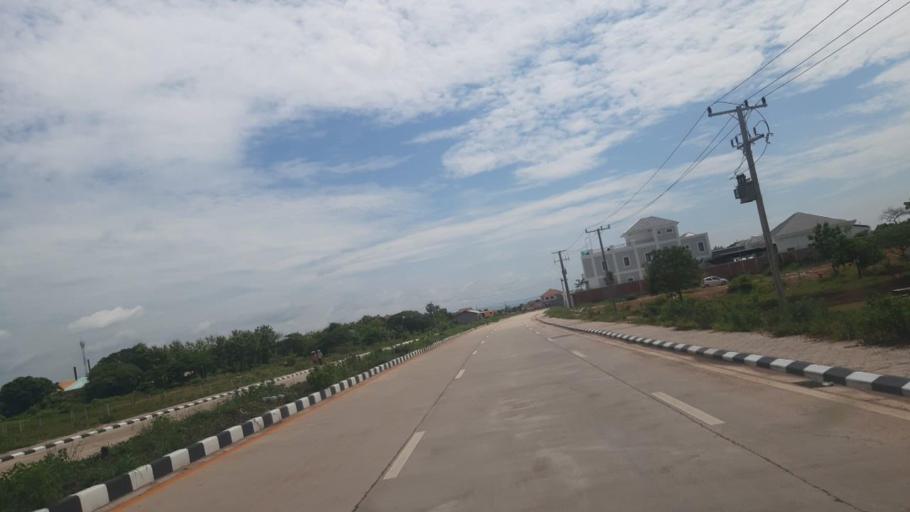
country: LA
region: Vientiane
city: Vientiane
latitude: 18.0355
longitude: 102.6119
